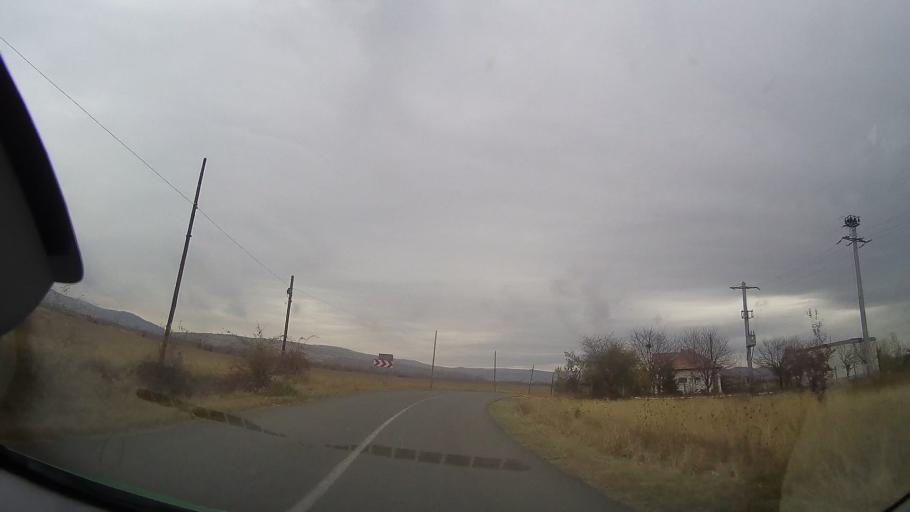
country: RO
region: Prahova
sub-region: Comuna Fantanele
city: Fantanele
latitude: 45.0216
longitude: 26.3805
